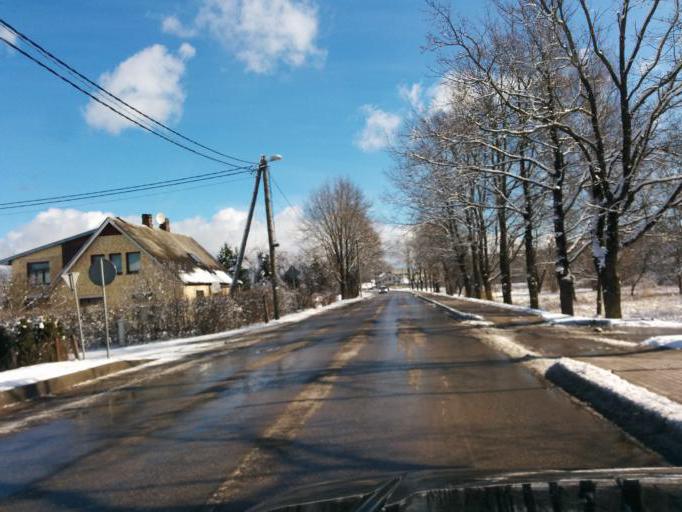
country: LV
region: Jelgava
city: Jelgava
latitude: 56.6289
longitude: 23.6939
